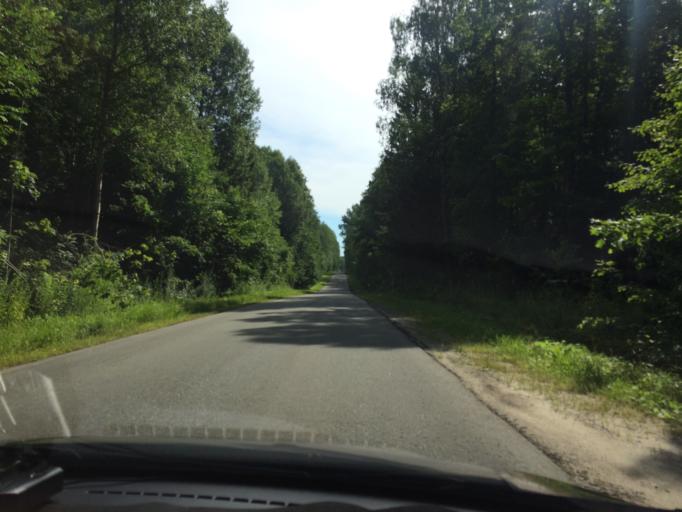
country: RU
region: Mariy-El
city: Surok
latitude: 56.5711
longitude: 48.1452
